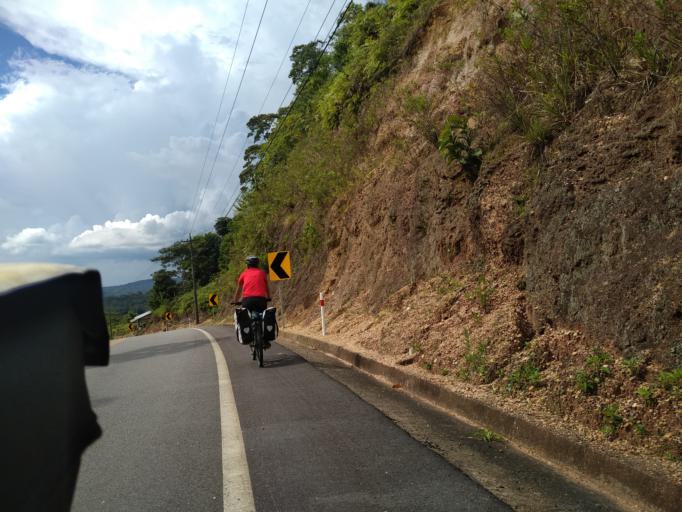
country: EC
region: Napo
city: Tena
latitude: -1.0796
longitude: -77.7912
